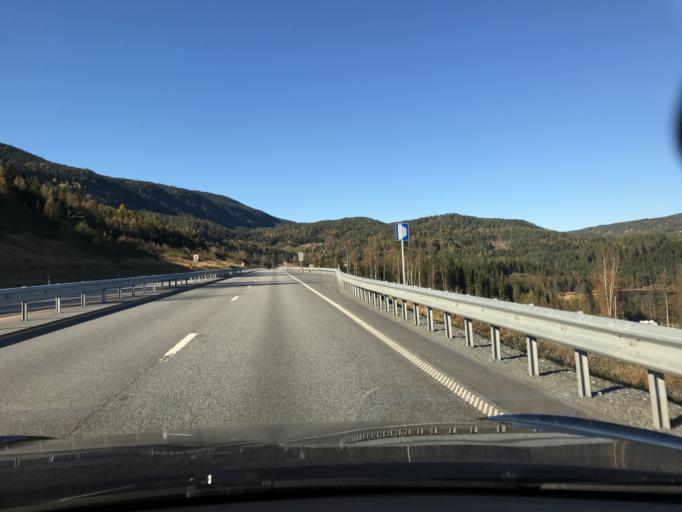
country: NO
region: Buskerud
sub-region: Krodsherad
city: Noresund
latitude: 60.2804
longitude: 9.7612
